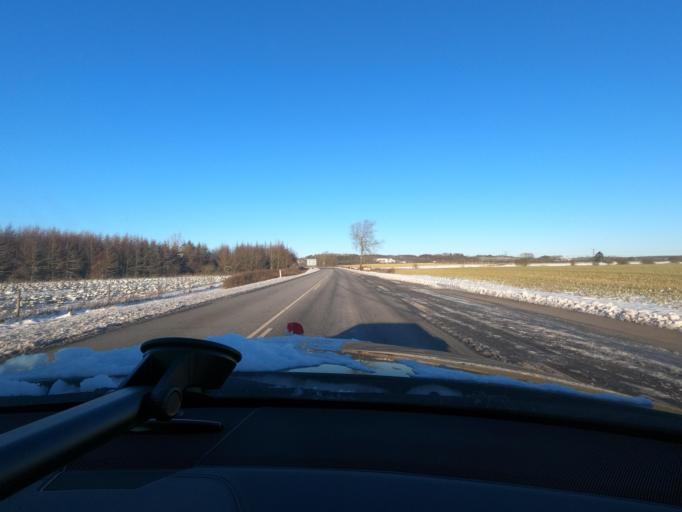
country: DK
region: South Denmark
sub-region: Aabenraa Kommune
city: Rodekro
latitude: 55.0777
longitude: 9.2205
